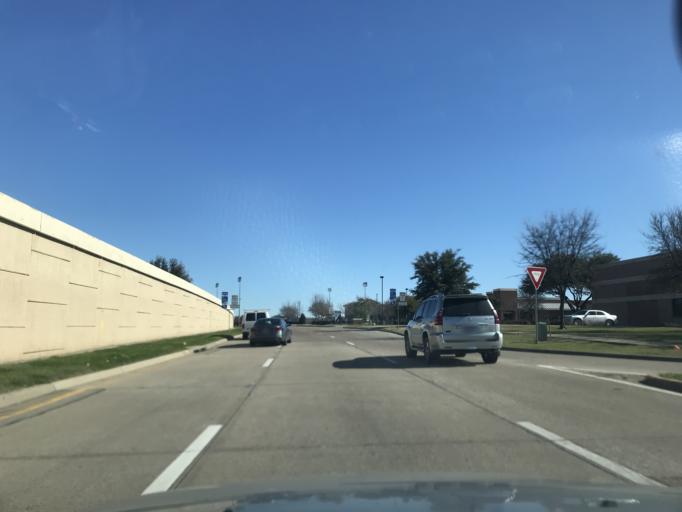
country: US
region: Texas
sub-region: Dallas County
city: Coppell
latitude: 32.9858
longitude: -96.9931
